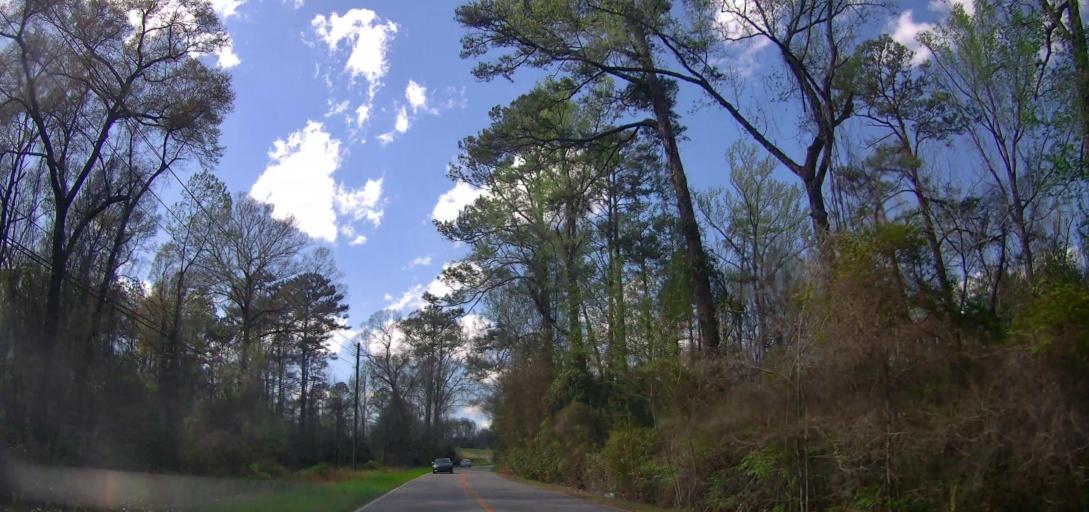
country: US
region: Georgia
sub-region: Bibb County
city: Macon
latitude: 32.8177
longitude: -83.5503
